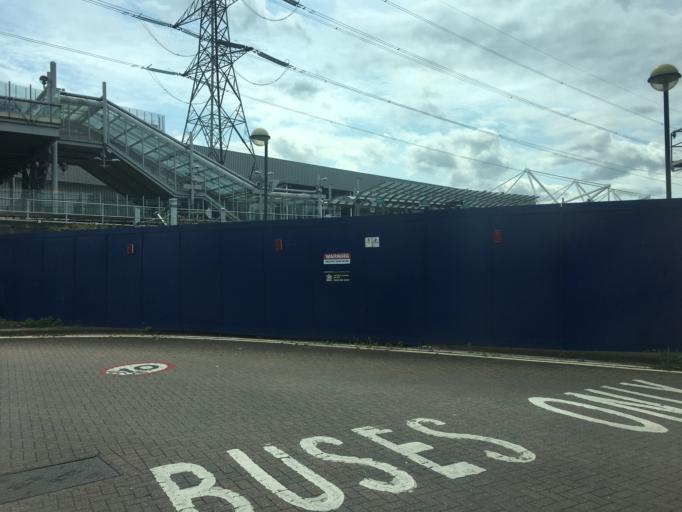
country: GB
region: England
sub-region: Greater London
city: East Ham
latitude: 51.5097
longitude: 0.0343
